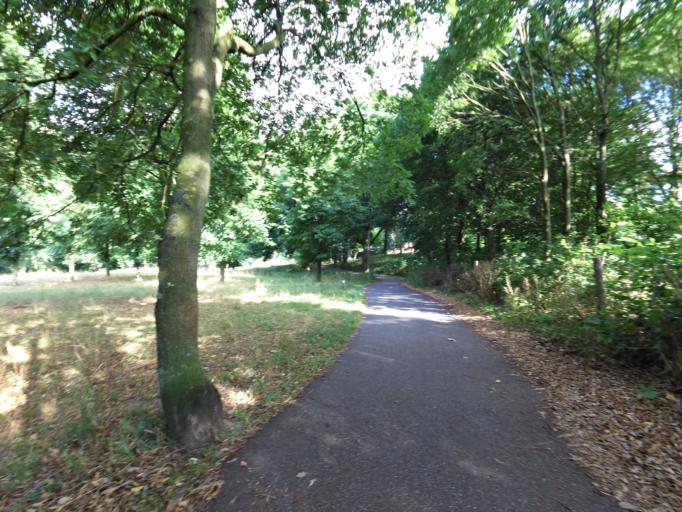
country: NL
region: Limburg
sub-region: Gemeente Heerlen
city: Heerlen
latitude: 50.8770
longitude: 5.9741
